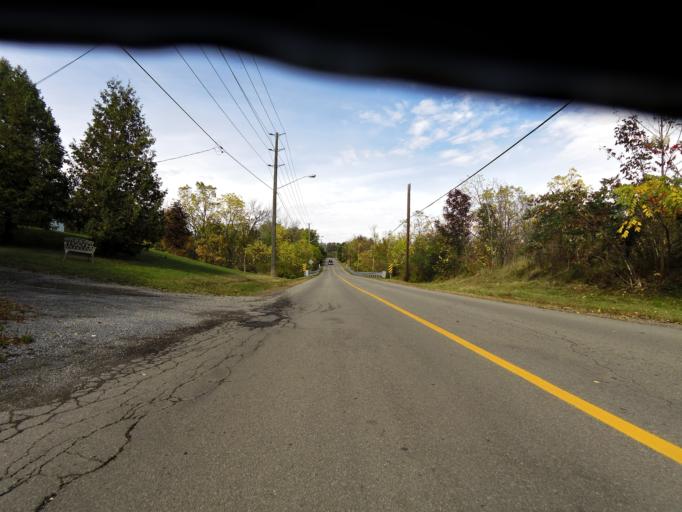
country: CA
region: Ontario
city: Hamilton
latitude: 43.2989
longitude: -79.9082
